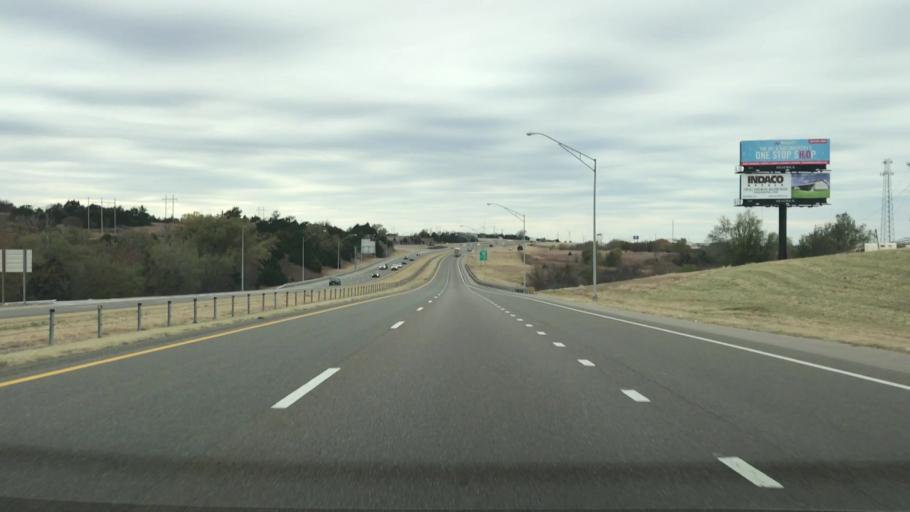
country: US
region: Oklahoma
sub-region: Custer County
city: Weatherford
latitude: 35.5213
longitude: -98.7177
